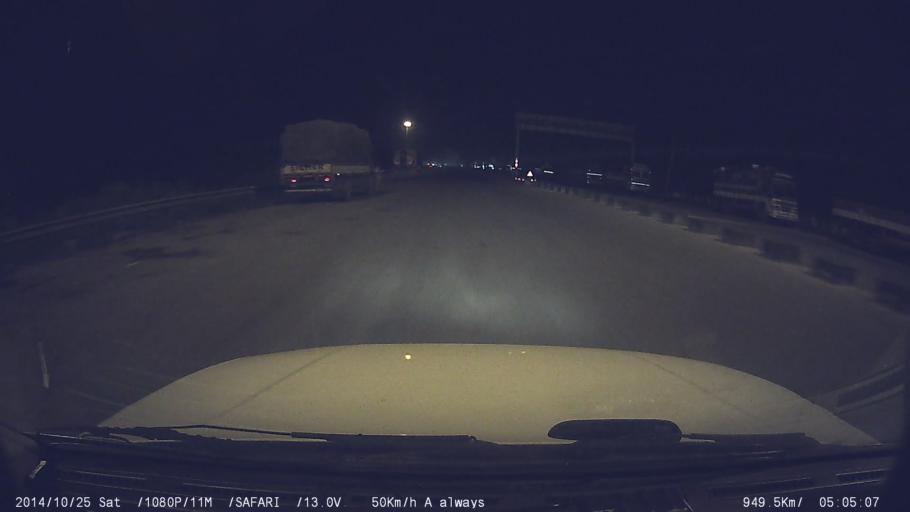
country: IN
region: Kerala
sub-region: Thrissur District
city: Trichur
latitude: 10.4418
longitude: 76.2610
